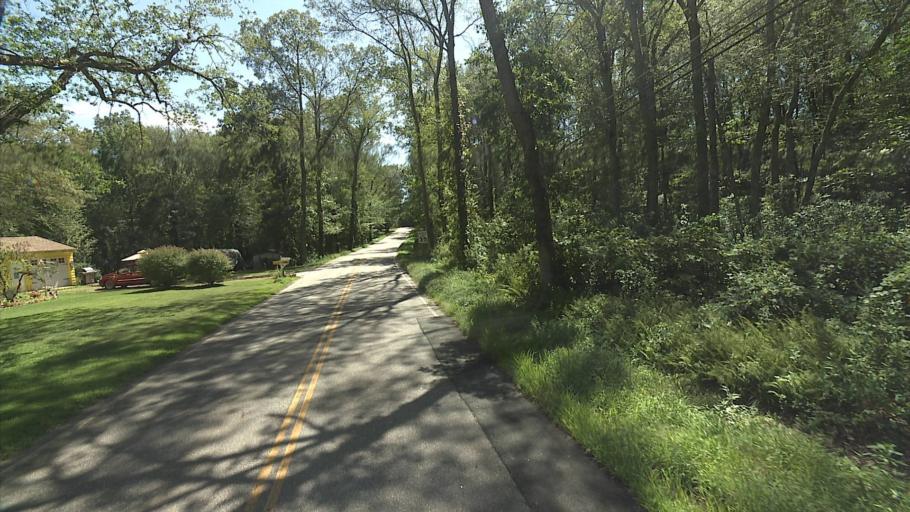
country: US
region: Connecticut
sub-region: Windham County
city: Windham
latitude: 41.7420
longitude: -72.0663
